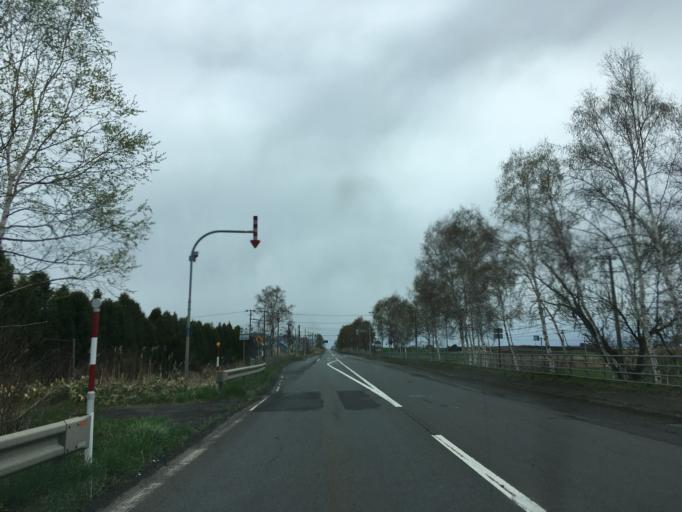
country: JP
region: Hokkaido
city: Chitose
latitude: 42.9140
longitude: 141.8106
